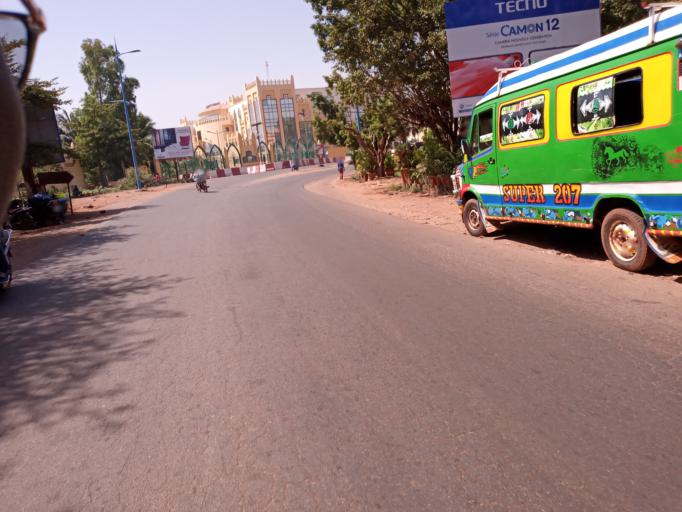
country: ML
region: Bamako
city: Bamako
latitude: 12.6278
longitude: -8.0082
